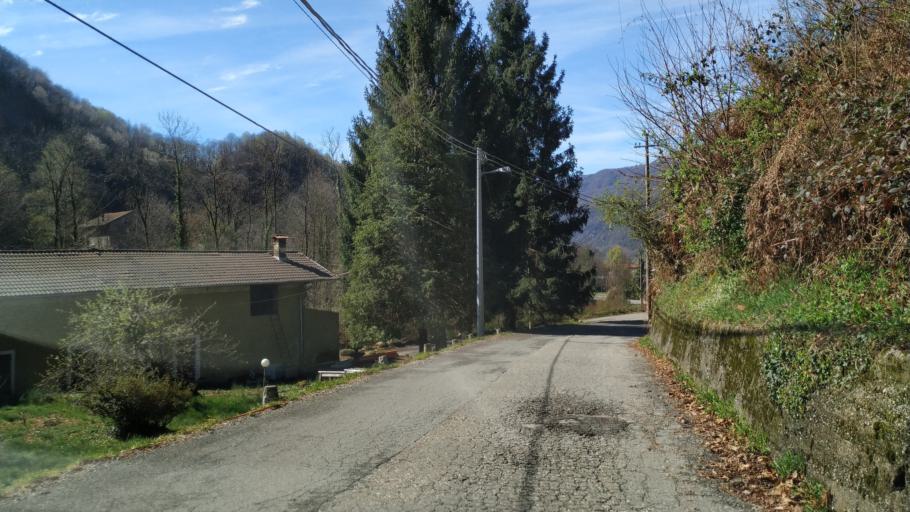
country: IT
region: Piedmont
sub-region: Provincia di Vercelli
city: Civiasco
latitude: 45.7971
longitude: 8.2837
